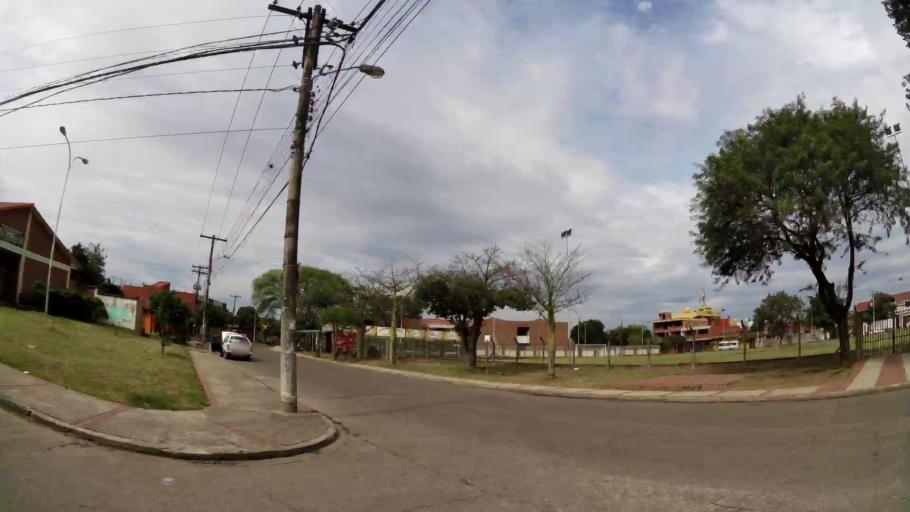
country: BO
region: Santa Cruz
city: Santa Cruz de la Sierra
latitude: -17.7877
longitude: -63.1997
